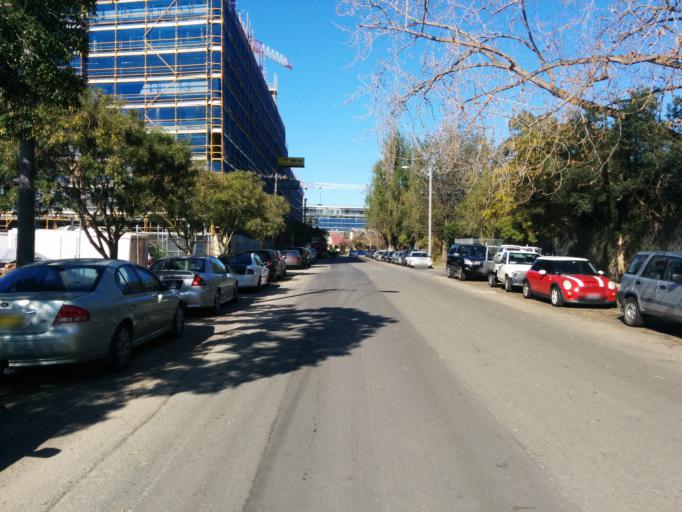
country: AU
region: New South Wales
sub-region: City of Sydney
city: Alexandria
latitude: -33.9084
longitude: 151.2059
